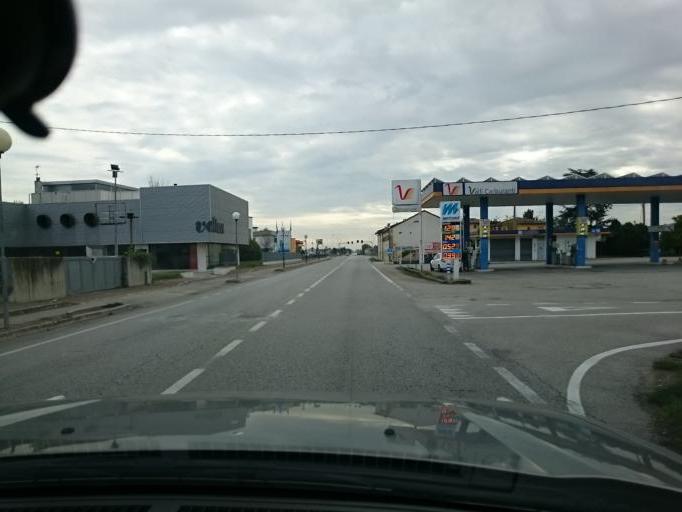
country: IT
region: Veneto
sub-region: Provincia di Padova
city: Sant'Angelo di Piove di Sacco
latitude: 45.3180
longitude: 12.0041
